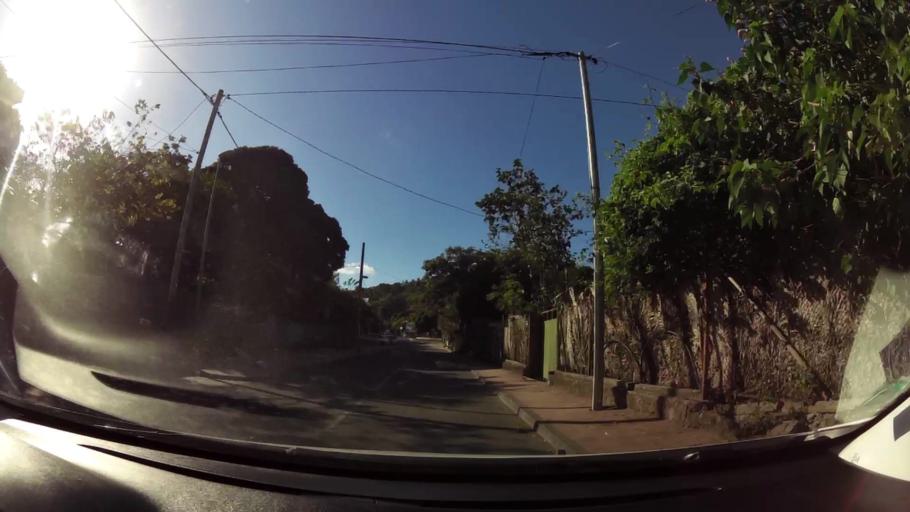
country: YT
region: Pamandzi
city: Pamandzi
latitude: -12.7972
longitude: 45.2743
